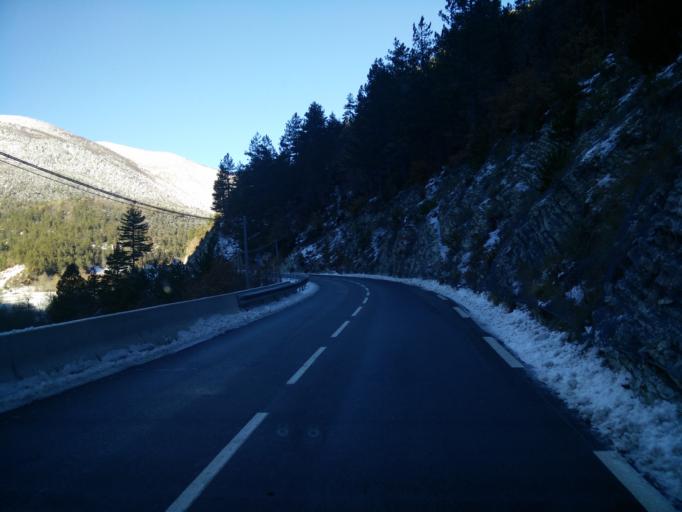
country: FR
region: Provence-Alpes-Cote d'Azur
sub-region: Departement des Alpes-de-Haute-Provence
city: Annot
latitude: 43.9305
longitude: 6.6432
